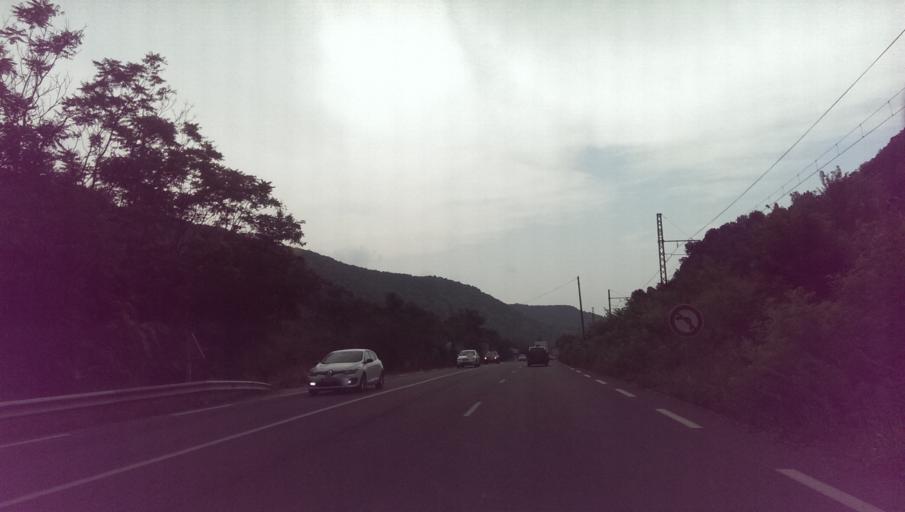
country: FR
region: Languedoc-Roussillon
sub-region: Departement des Pyrenees-Orientales
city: Ria-Sirach
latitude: 42.5979
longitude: 2.3784
